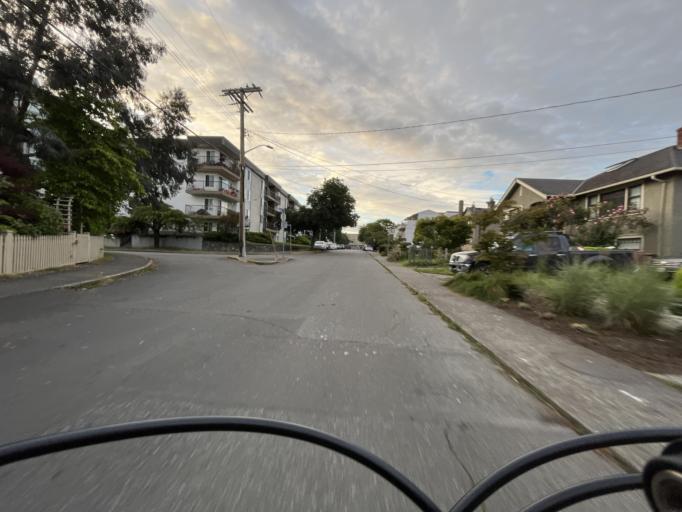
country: CA
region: British Columbia
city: Victoria
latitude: 48.4294
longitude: -123.3888
